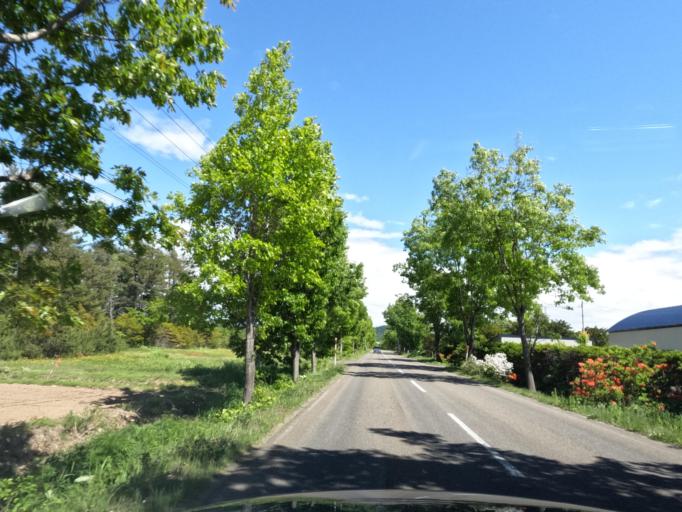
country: JP
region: Hokkaido
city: Kitahiroshima
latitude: 43.0211
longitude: 141.7097
